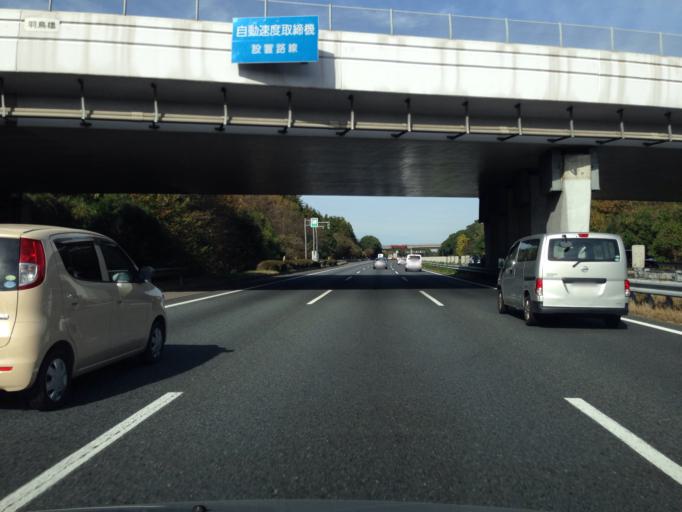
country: JP
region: Ibaraki
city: Ishioka
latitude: 36.2483
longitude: 140.2970
